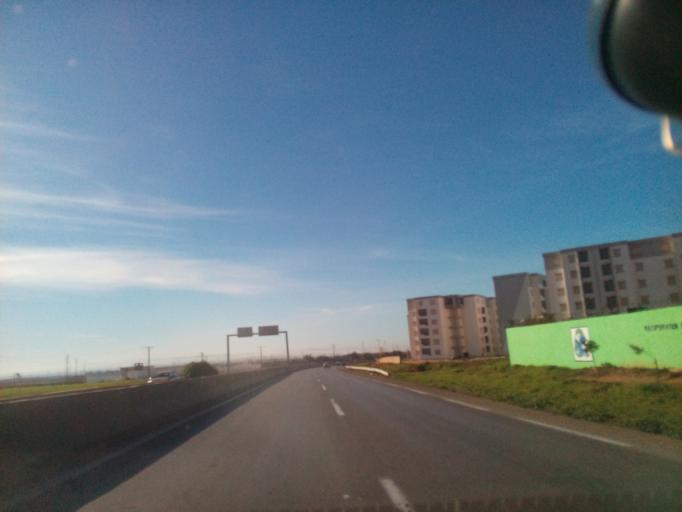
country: DZ
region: Oran
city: Ain el Bya
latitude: 35.7816
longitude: -0.4130
